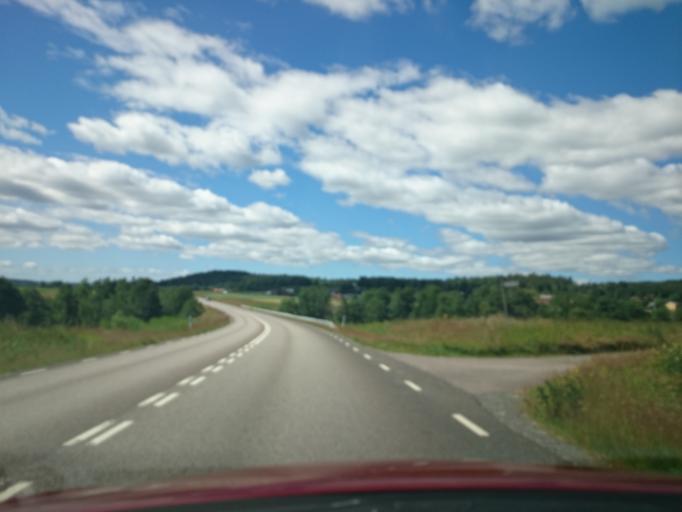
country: SE
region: Vaestra Goetaland
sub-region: Lerums Kommun
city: Olstorp
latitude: 57.8260
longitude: 12.2193
